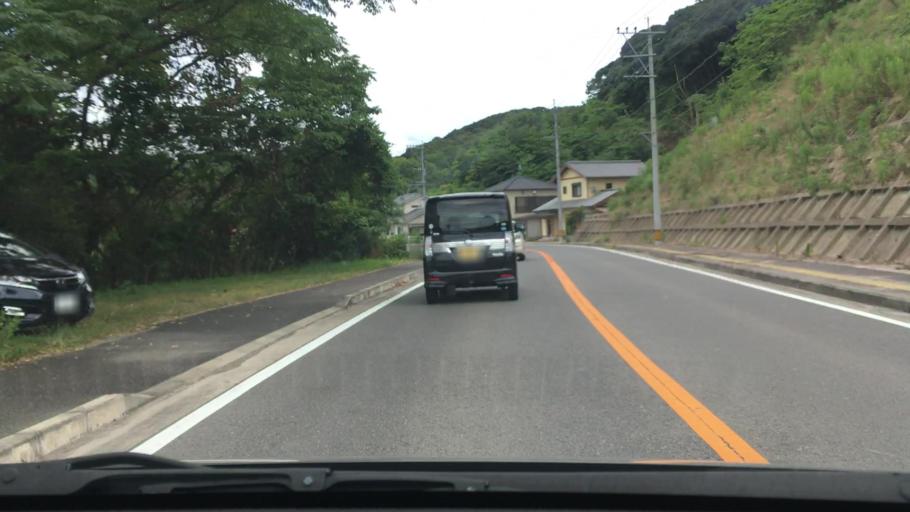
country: JP
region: Nagasaki
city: Togitsu
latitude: 32.9868
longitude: 129.7752
